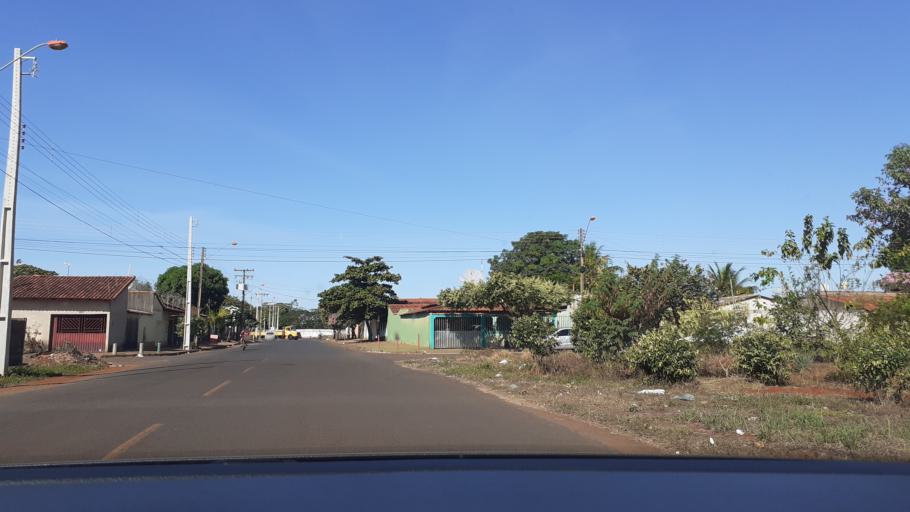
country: BR
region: Goias
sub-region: Itumbiara
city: Itumbiara
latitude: -18.4112
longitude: -49.2583
